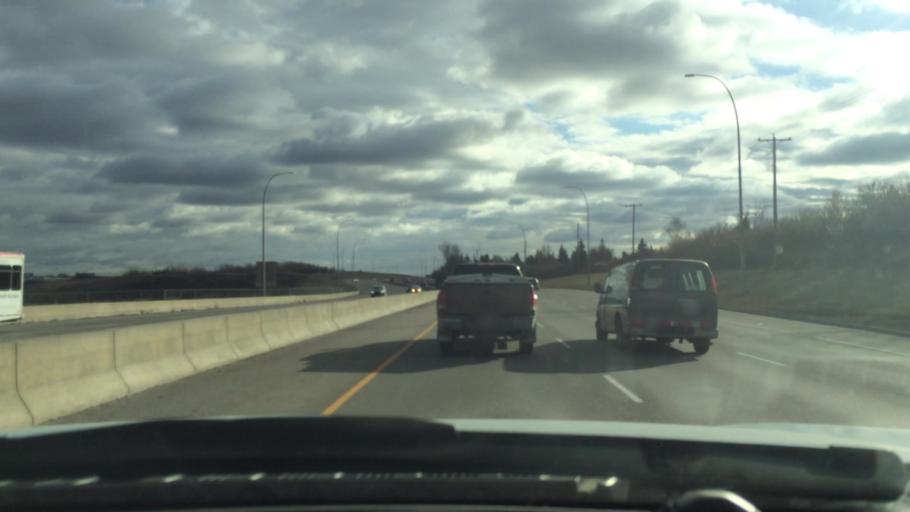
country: CA
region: Alberta
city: Calgary
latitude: 51.1319
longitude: -114.0646
